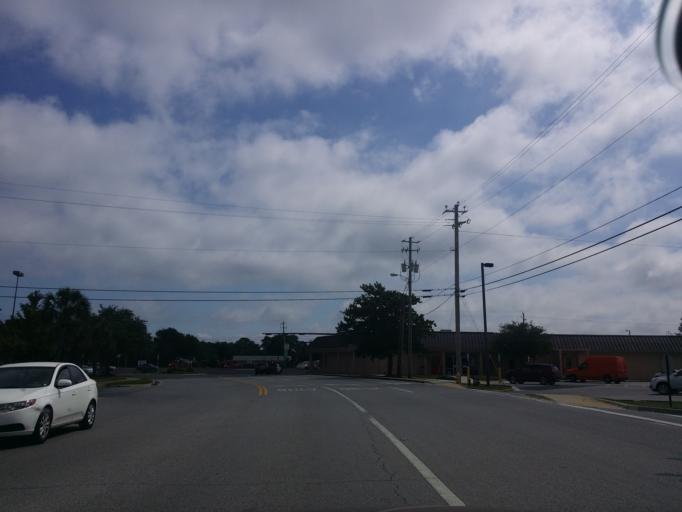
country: US
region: Florida
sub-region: Santa Rosa County
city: Gulf Breeze
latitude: 30.3651
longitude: -87.1712
